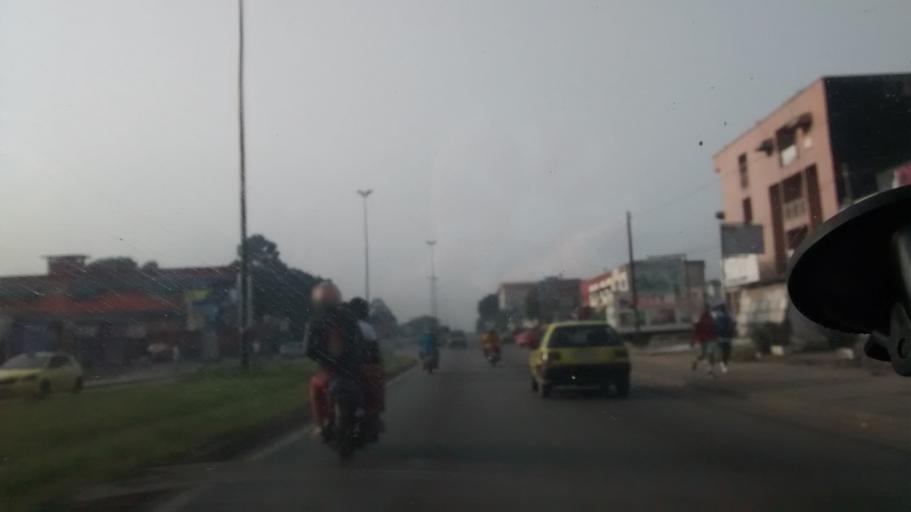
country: CI
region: Lagunes
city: Abobo
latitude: 5.3955
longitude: -3.9919
